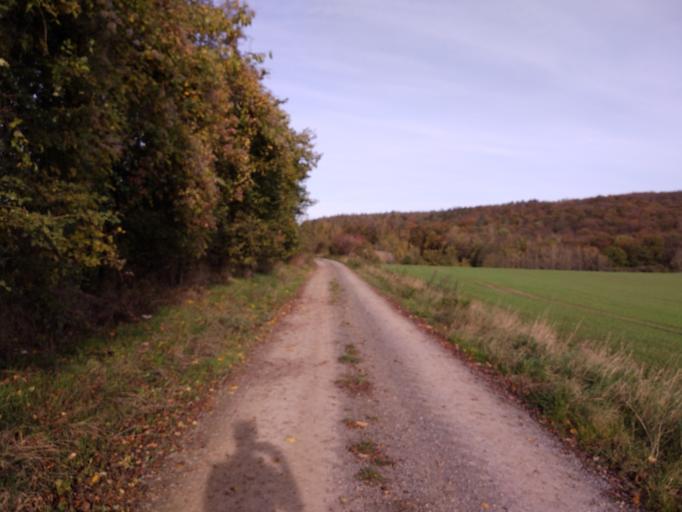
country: DE
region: North Rhine-Westphalia
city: Beverungen
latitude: 51.6840
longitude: 9.3532
